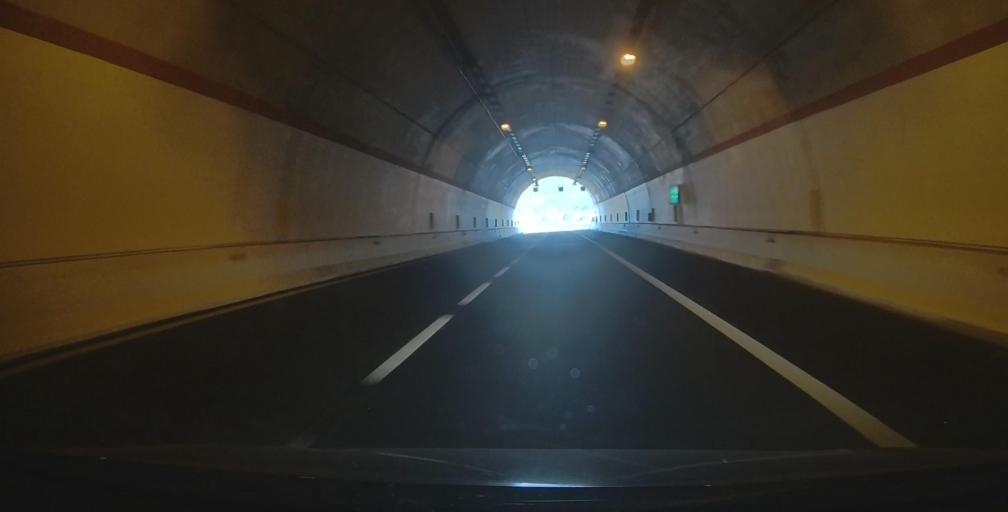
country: IT
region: Basilicate
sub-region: Provincia di Potenza
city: Castelluccio Superiore
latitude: 40.0109
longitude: 15.9015
